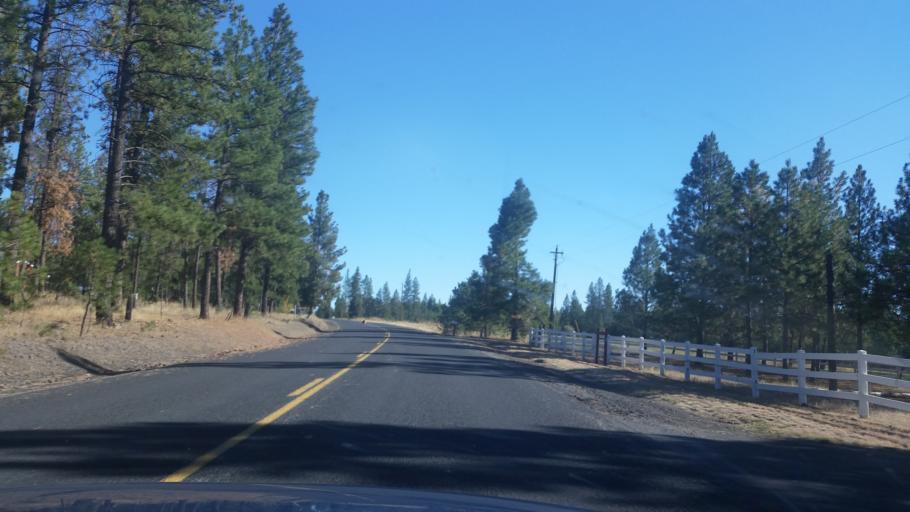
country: US
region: Washington
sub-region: Spokane County
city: Cheney
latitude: 47.5475
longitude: -117.4826
